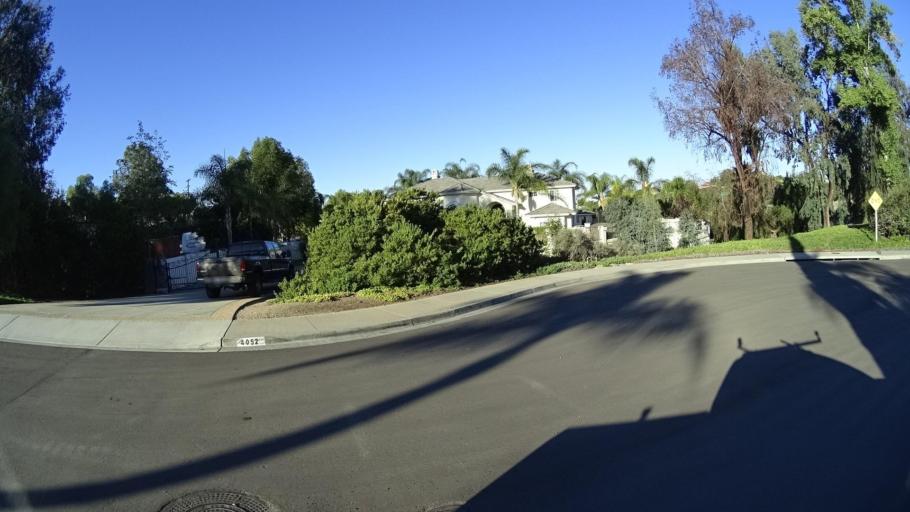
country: US
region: California
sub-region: San Diego County
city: Bonita
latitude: 32.6684
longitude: -117.0444
